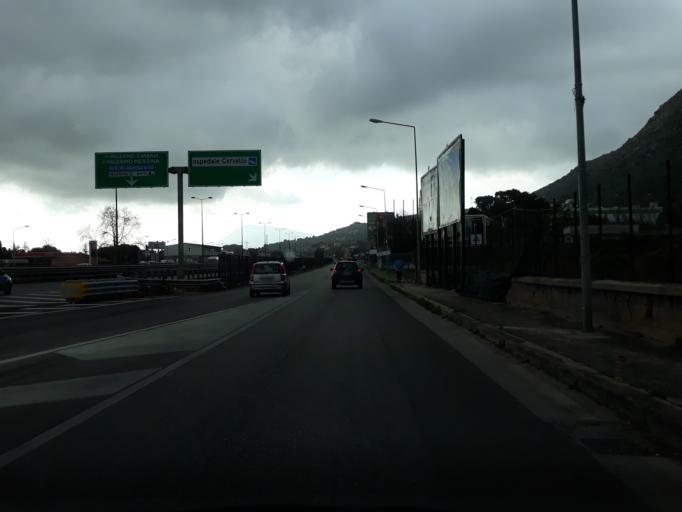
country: IT
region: Sicily
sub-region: Palermo
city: Isola delle Femmine
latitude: 38.1805
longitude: 13.2920
